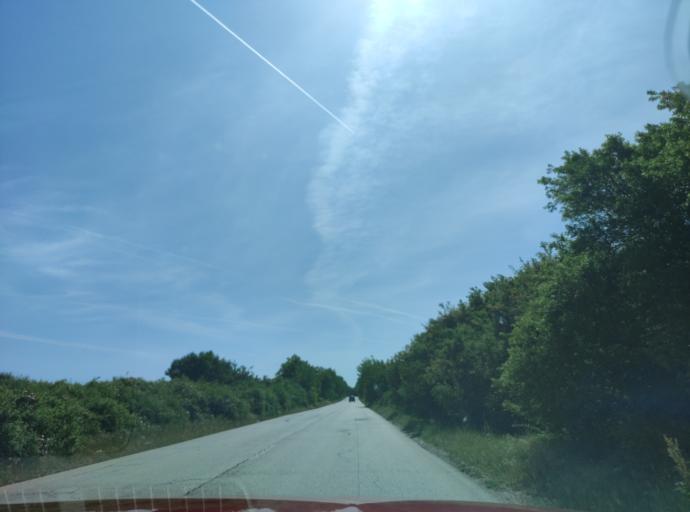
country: BG
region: Pleven
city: Iskur
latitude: 43.4491
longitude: 24.3204
